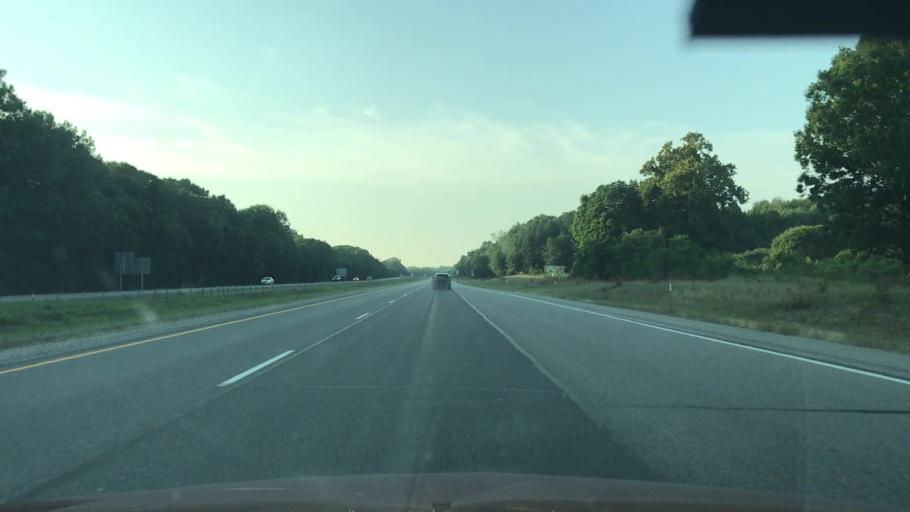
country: US
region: Michigan
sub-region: Allegan County
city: Douglas
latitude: 42.5981
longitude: -86.2172
